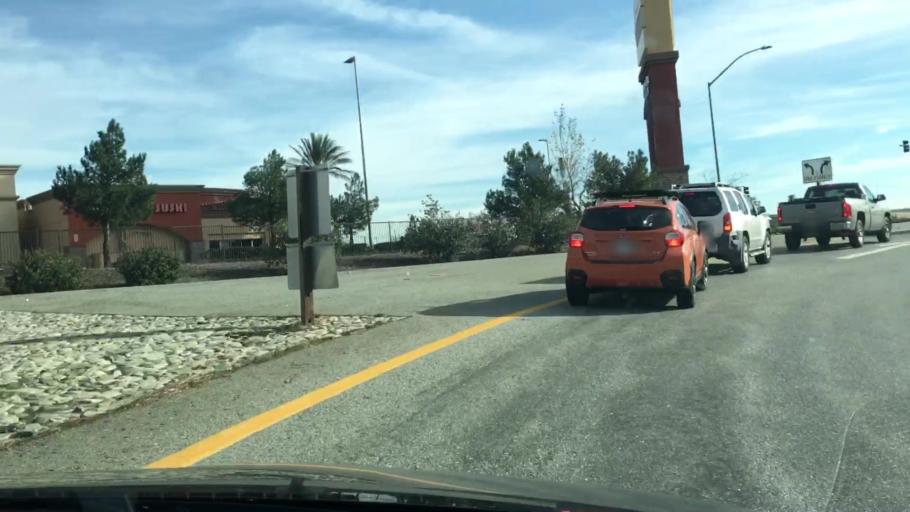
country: US
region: California
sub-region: San Bernardino County
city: Fontana
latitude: 34.1512
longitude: -117.4765
